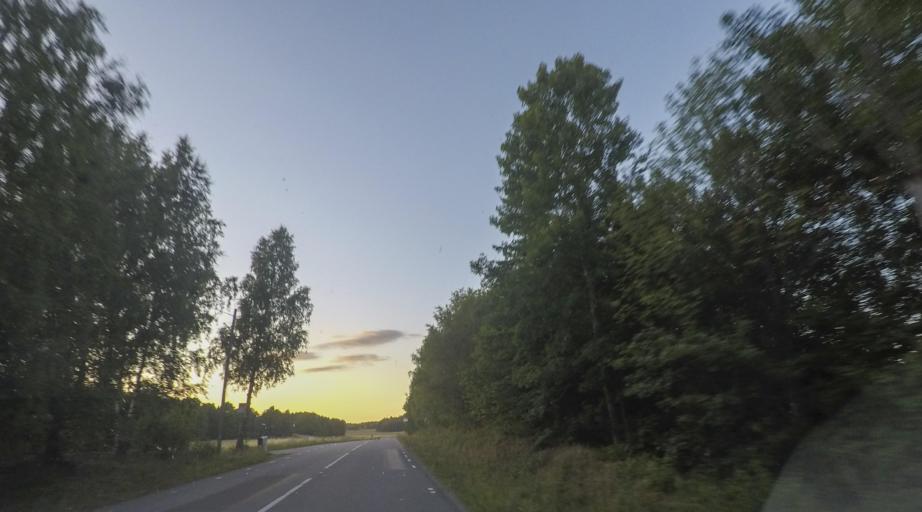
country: SE
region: Soedermanland
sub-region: Trosa Kommun
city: Trosa
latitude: 58.9761
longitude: 17.6929
